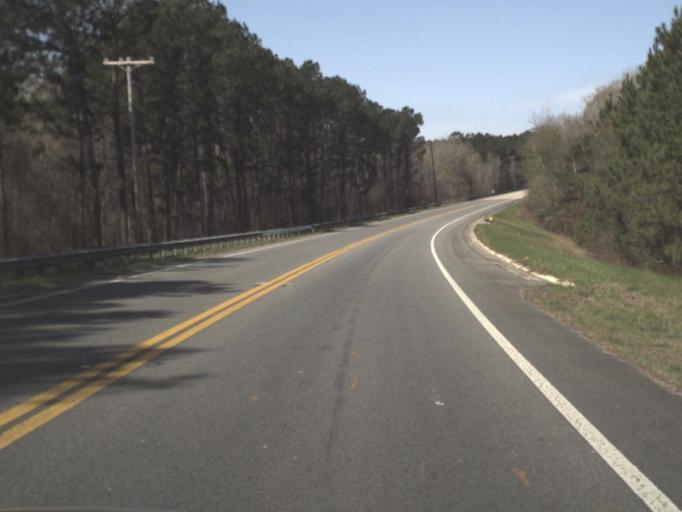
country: US
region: Florida
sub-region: Gadsden County
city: Havana
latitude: 30.5866
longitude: -84.4936
